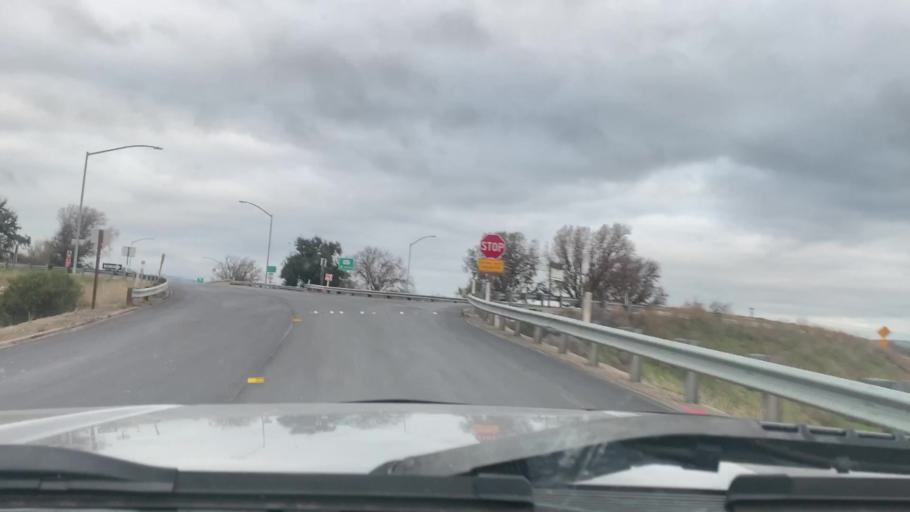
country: US
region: California
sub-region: San Luis Obispo County
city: Templeton
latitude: 35.5649
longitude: -120.7010
